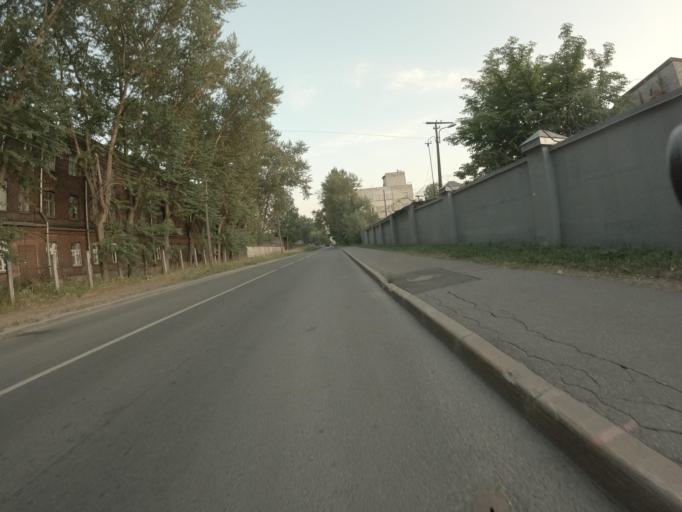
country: RU
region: St.-Petersburg
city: Kupchino
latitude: 59.8926
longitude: 30.3381
